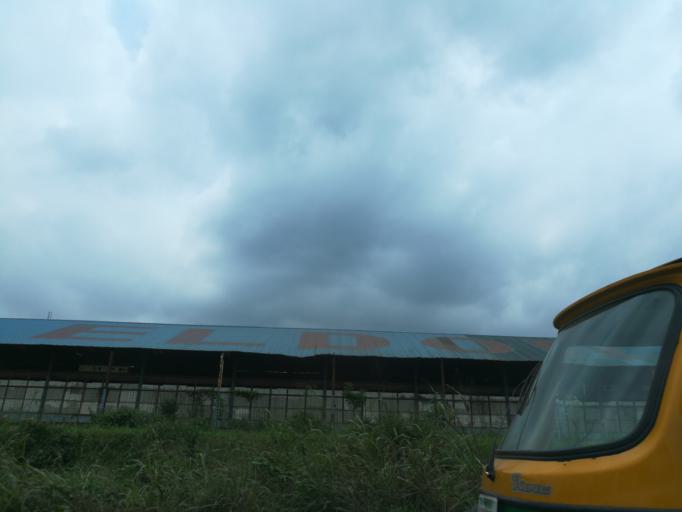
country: NG
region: Lagos
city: Agege
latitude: 6.6044
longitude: 3.3320
